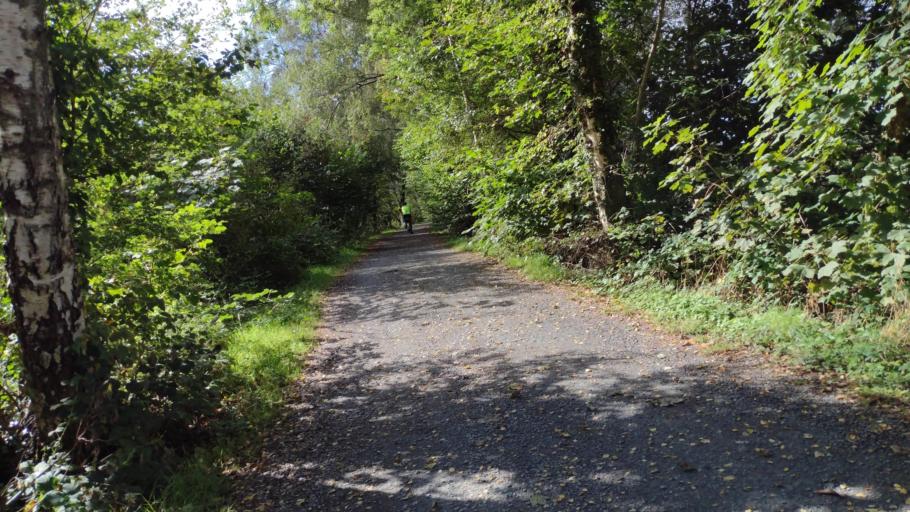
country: GB
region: Wales
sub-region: Gwynedd
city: Barmouth
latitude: 52.7068
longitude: -4.0226
